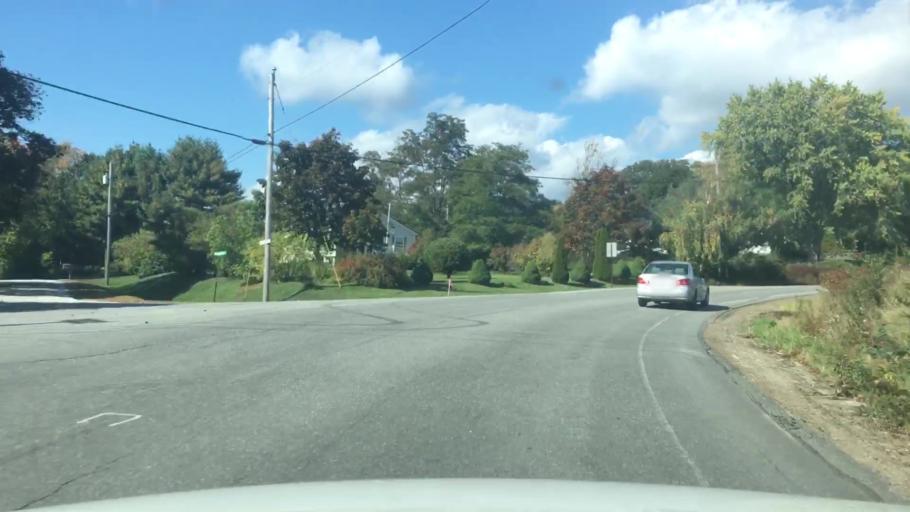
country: US
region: Maine
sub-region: Knox County
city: Warren
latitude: 44.1257
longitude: -69.2401
